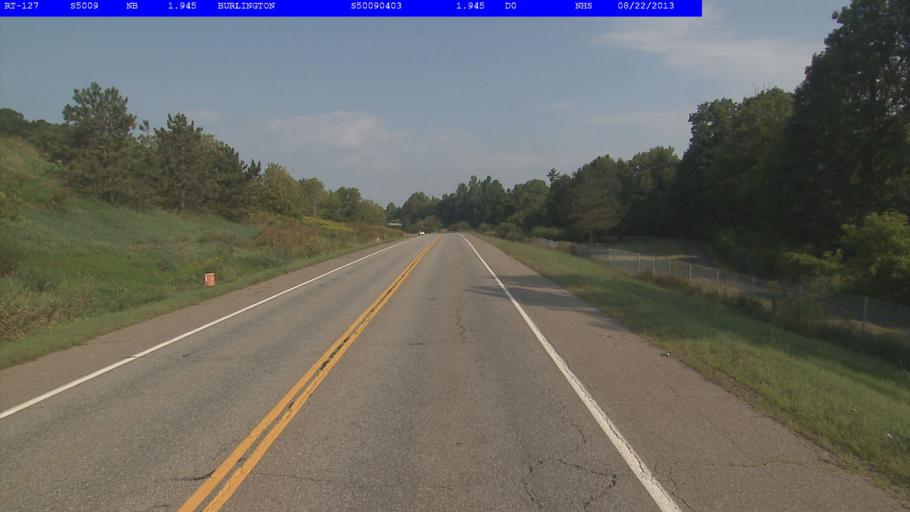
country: US
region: Vermont
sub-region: Chittenden County
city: Burlington
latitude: 44.5123
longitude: -73.2343
